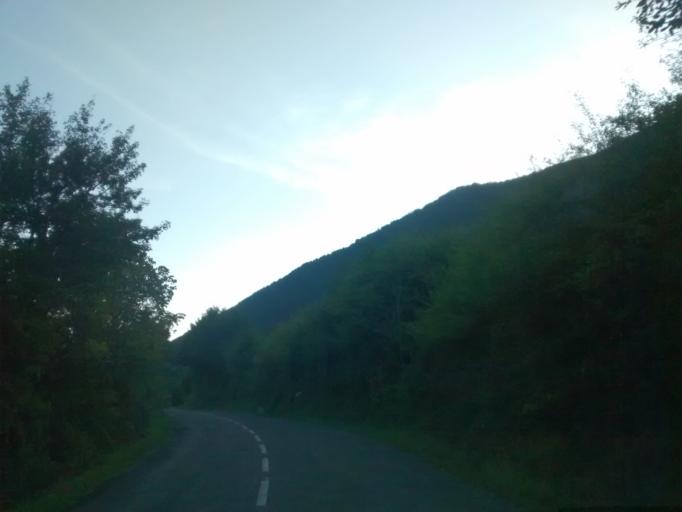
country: ES
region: Aragon
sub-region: Provincia de Huesca
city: Anso
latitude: 42.7770
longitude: -0.7424
